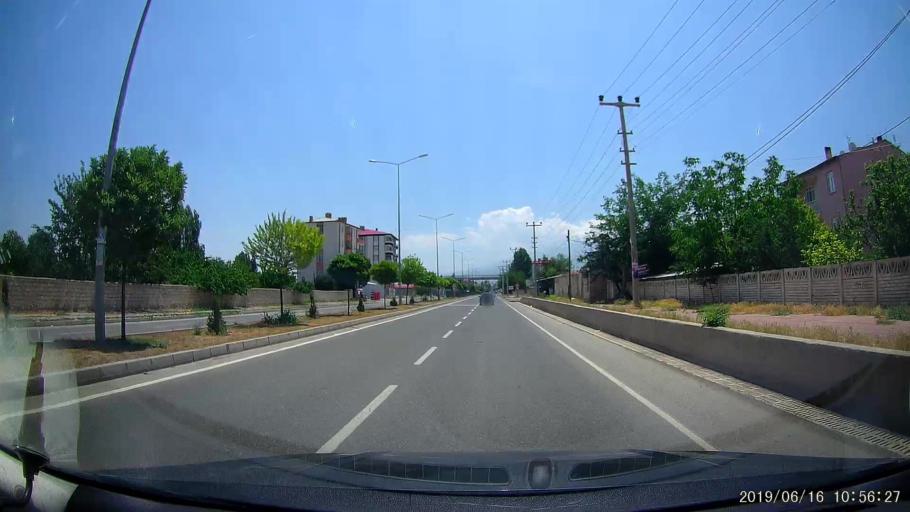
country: TR
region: Igdir
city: Igdir
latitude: 39.9296
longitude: 44.0226
